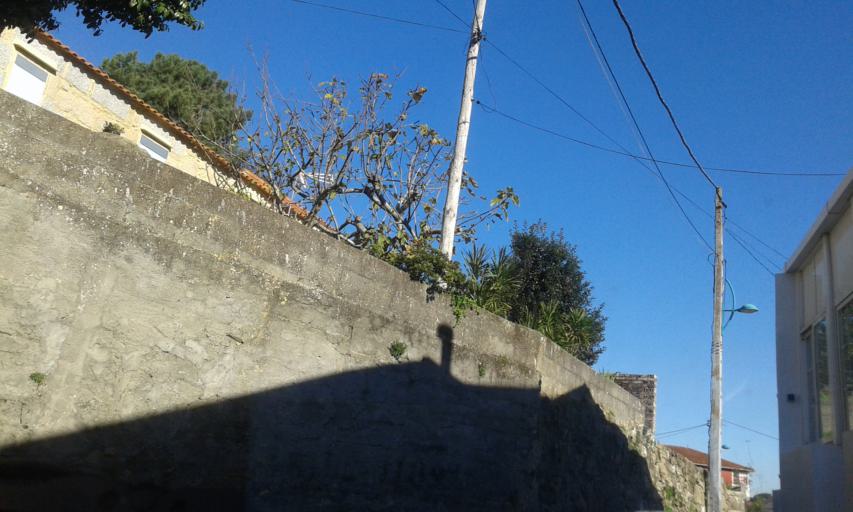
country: ES
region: Galicia
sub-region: Provincia de Pontevedra
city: Marin
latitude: 42.3693
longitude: -8.7370
